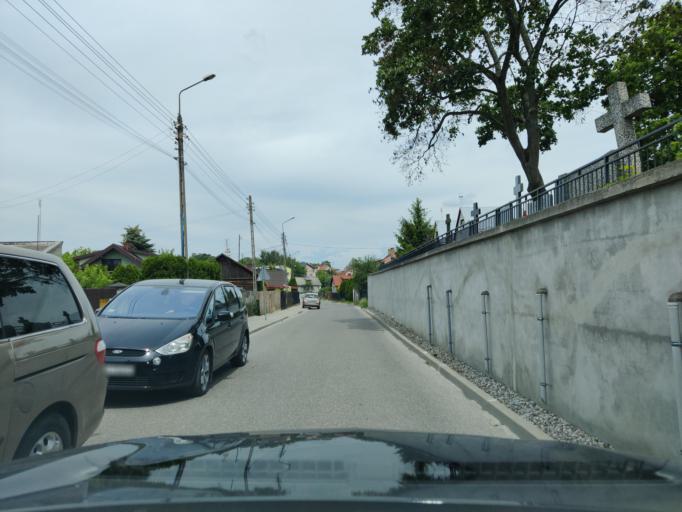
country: PL
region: Masovian Voivodeship
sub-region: Powiat wyszkowski
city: Wyszkow
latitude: 52.5983
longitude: 21.4587
